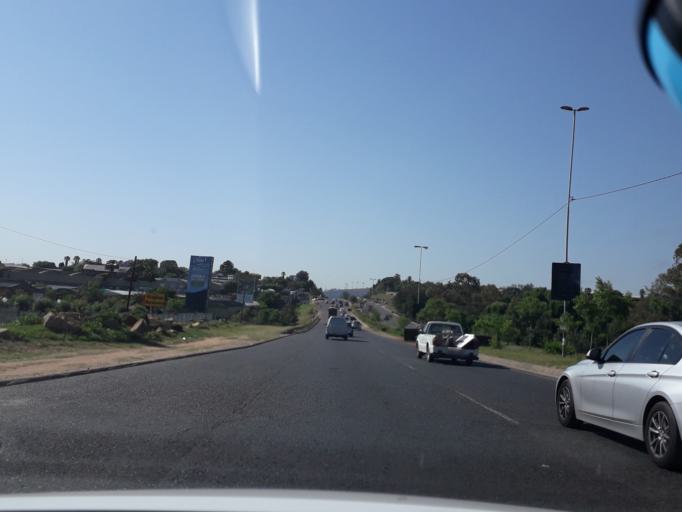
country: ZA
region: Gauteng
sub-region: City of Johannesburg Metropolitan Municipality
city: Roodepoort
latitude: -26.0937
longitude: 27.9398
